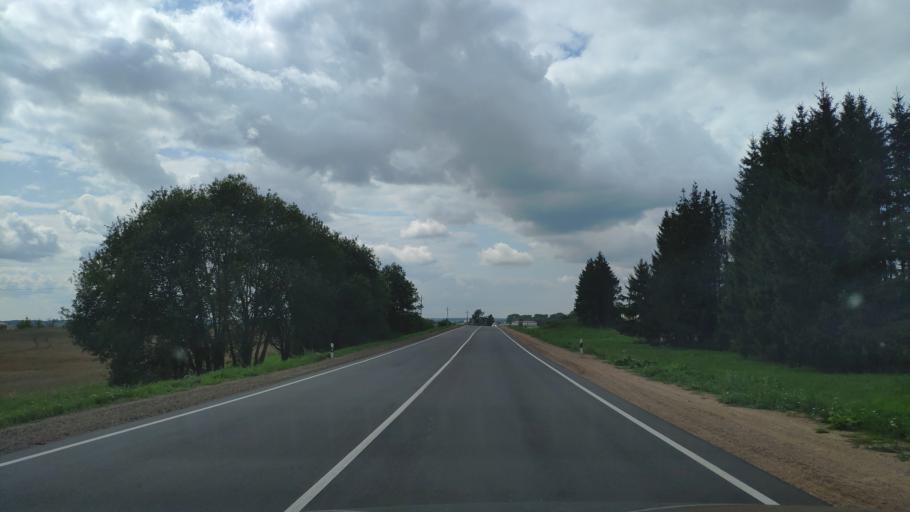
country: BY
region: Minsk
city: Zaslawye
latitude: 54.0051
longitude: 27.3548
